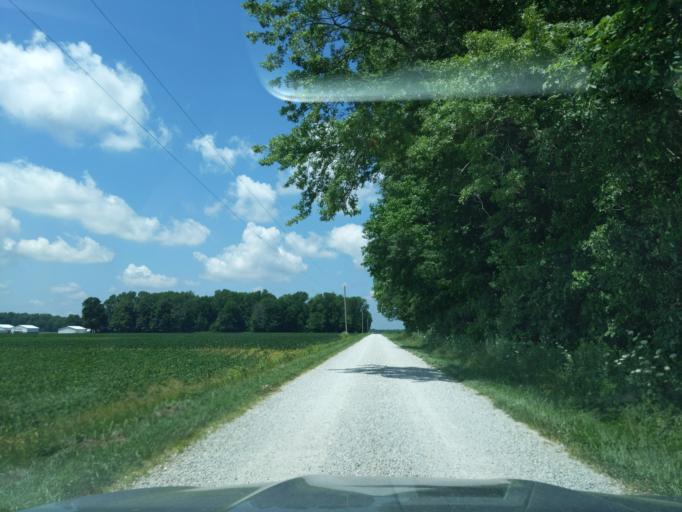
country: US
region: Indiana
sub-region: Ripley County
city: Osgood
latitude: 39.2209
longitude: -85.3587
